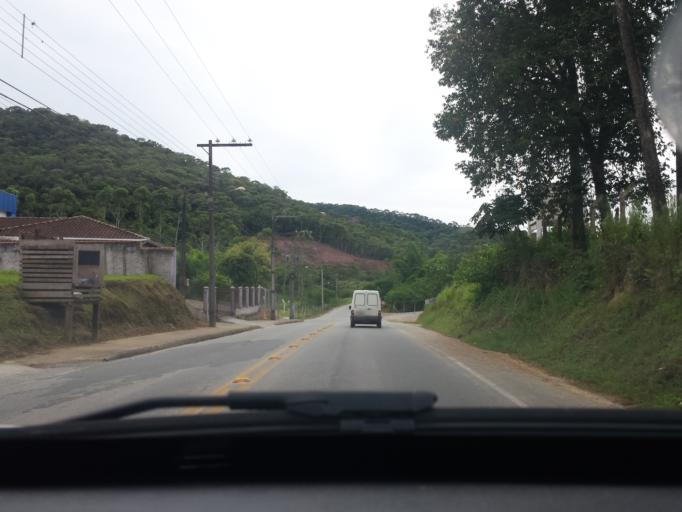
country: BR
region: Santa Catarina
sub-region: Gaspar
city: Gaspar
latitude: -26.8895
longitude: -48.9946
